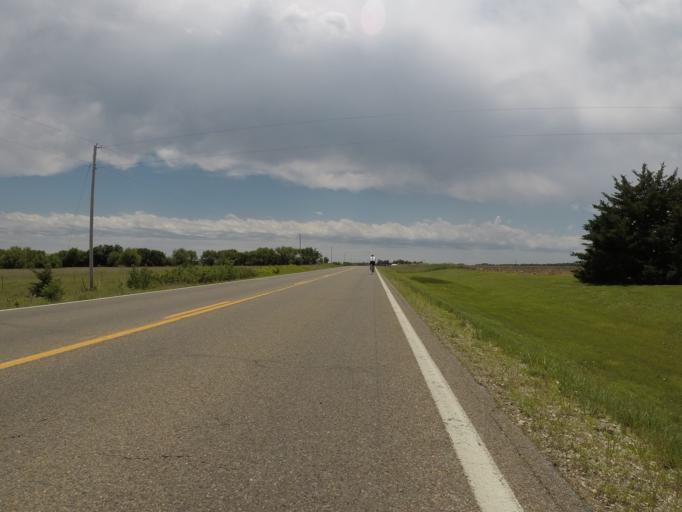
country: US
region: Kansas
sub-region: Morris County
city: Council Grove
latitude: 38.8207
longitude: -96.5013
